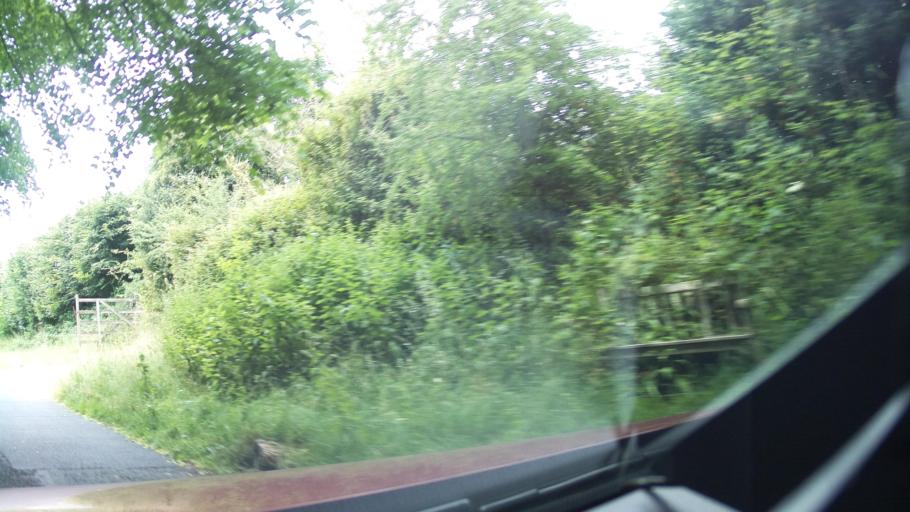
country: GB
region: England
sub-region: Devon
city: Totnes
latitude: 50.4394
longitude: -3.7069
